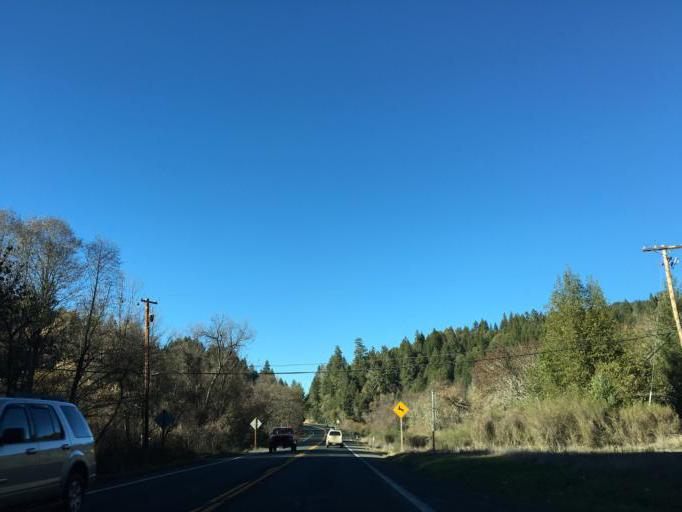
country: US
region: California
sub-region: Mendocino County
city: Brooktrails
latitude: 39.5109
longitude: -123.3861
